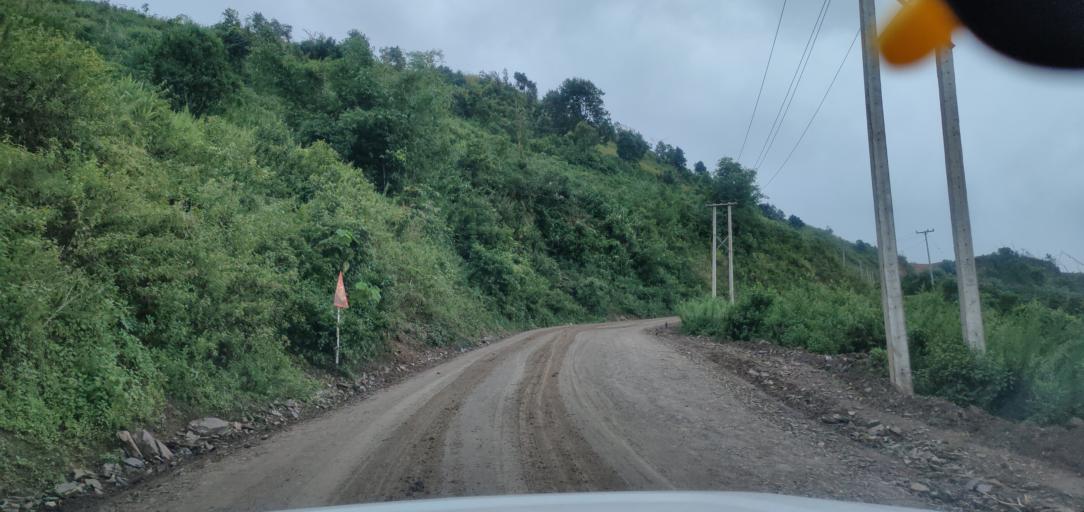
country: LA
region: Phongsali
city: Phongsali
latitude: 21.4271
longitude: 102.1694
